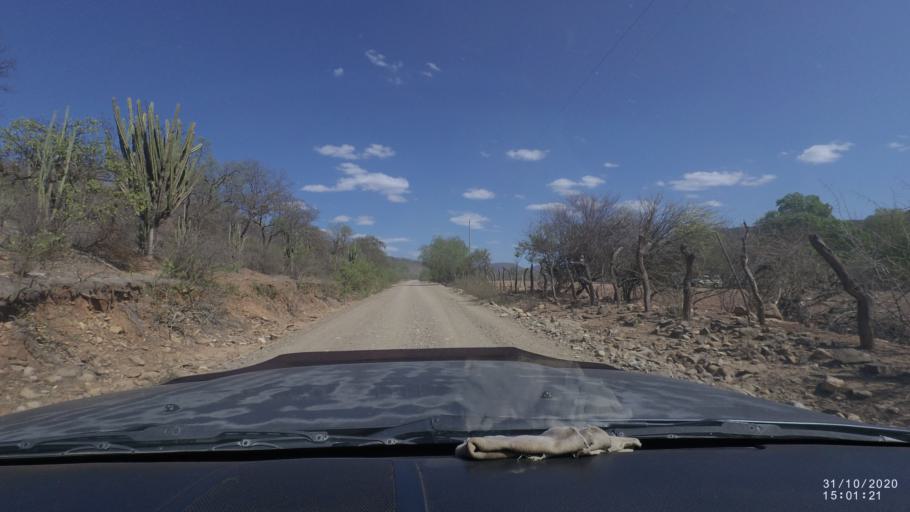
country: BO
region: Cochabamba
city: Aiquile
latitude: -18.2630
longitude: -64.8195
